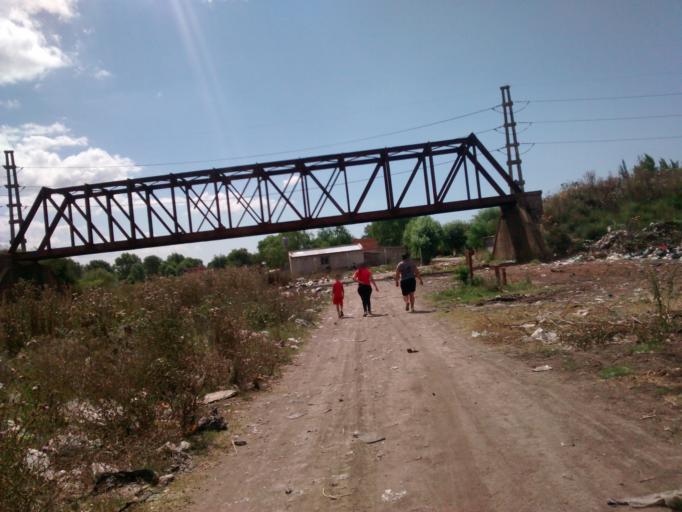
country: AR
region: Buenos Aires
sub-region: Partido de La Plata
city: La Plata
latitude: -34.9654
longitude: -57.9332
